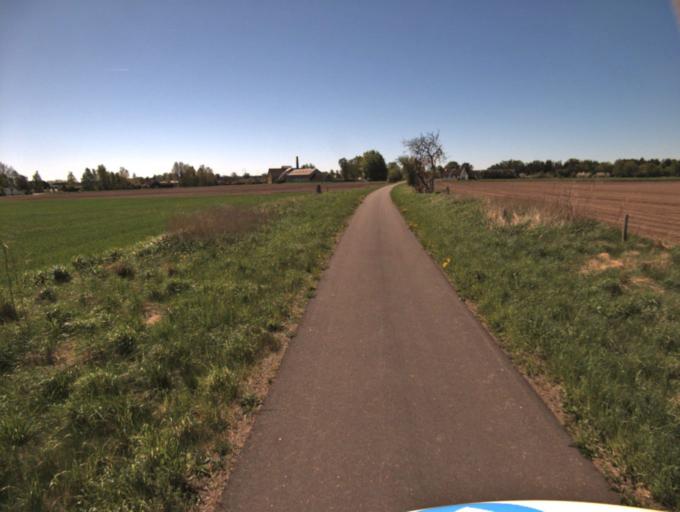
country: SE
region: Skane
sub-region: Kristianstads Kommun
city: Norra Asum
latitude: 55.9533
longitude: 14.1562
